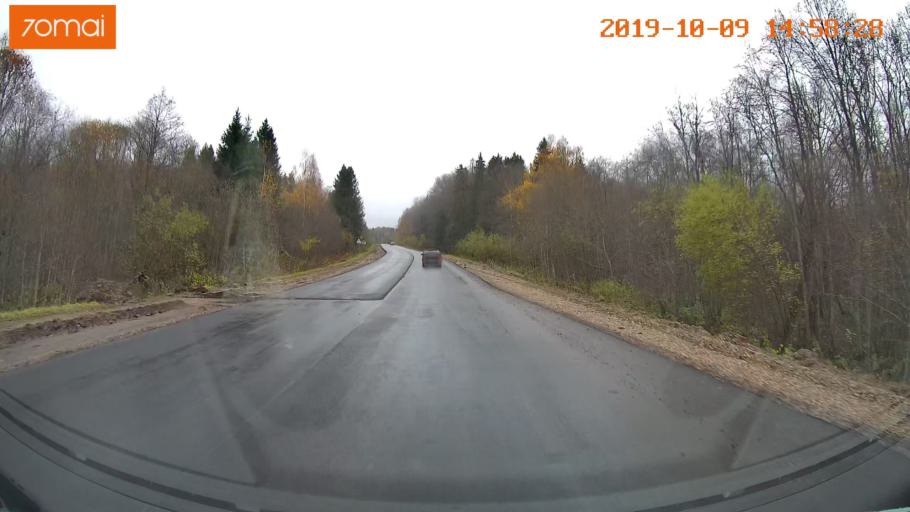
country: RU
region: Kostroma
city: Chistyye Bory
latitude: 58.3265
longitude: 41.6551
